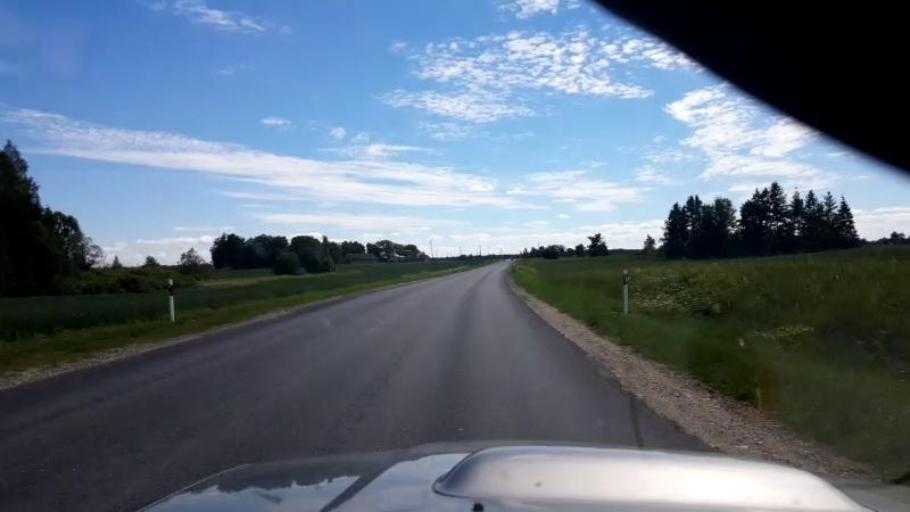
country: EE
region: Laeaene-Virumaa
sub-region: Rakke vald
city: Rakke
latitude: 58.9040
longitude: 26.2818
